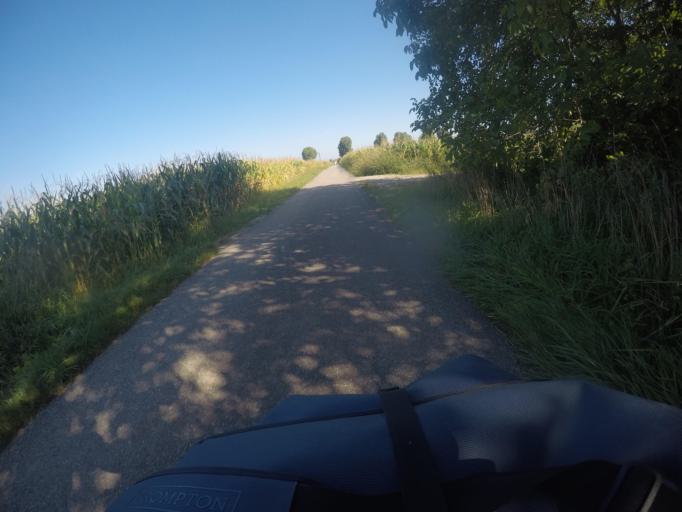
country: FR
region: Alsace
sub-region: Departement du Haut-Rhin
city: Ottmarsheim
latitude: 47.7809
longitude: 7.5056
